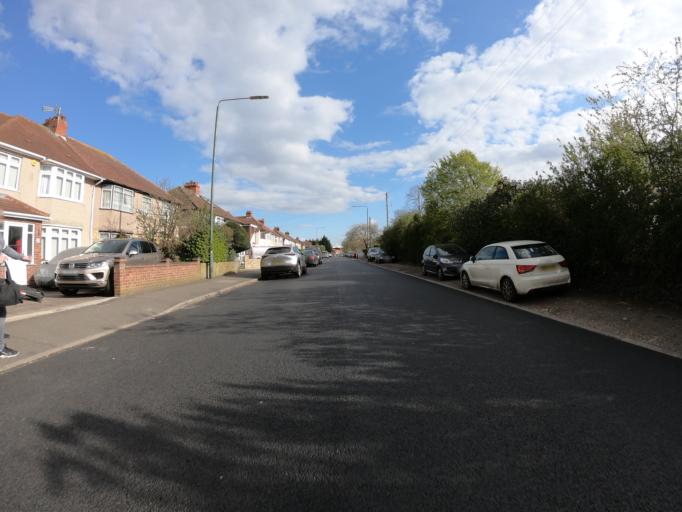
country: GB
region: England
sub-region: Greater London
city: Bexleyheath
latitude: 51.4630
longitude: 0.1513
